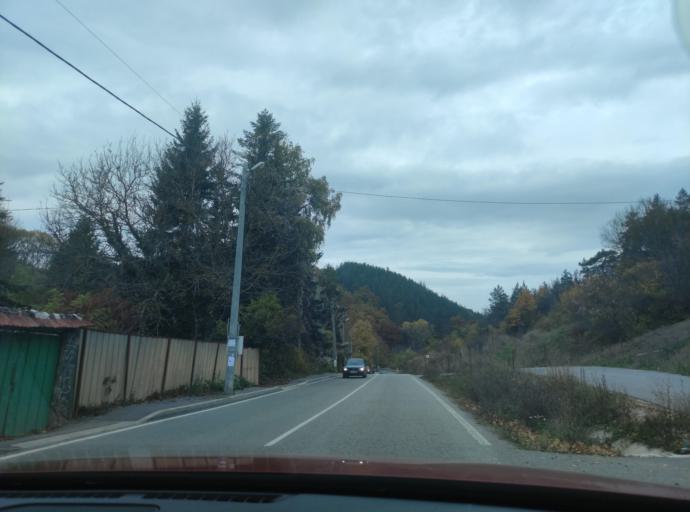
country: BG
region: Sofiya
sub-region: Obshtina Godech
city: Godech
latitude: 42.9738
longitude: 23.1396
